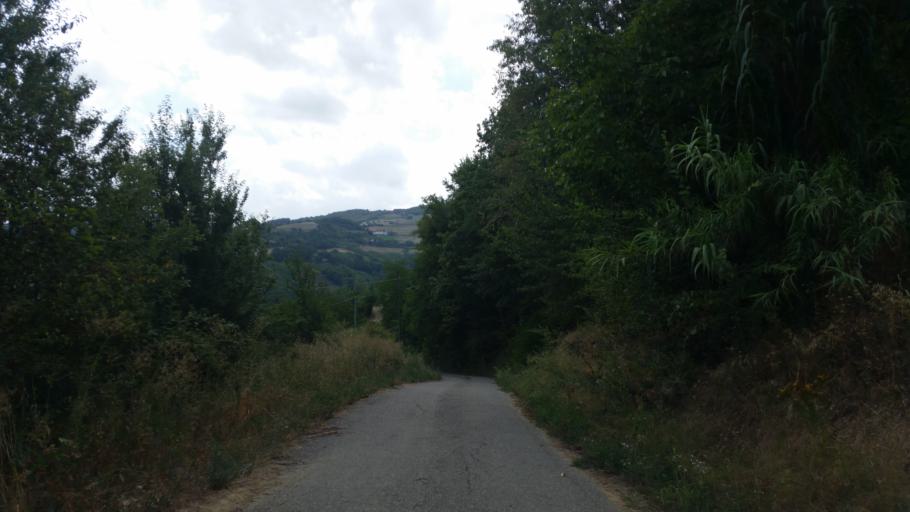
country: IT
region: Piedmont
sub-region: Provincia di Asti
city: Bubbio
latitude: 44.6355
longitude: 8.2847
